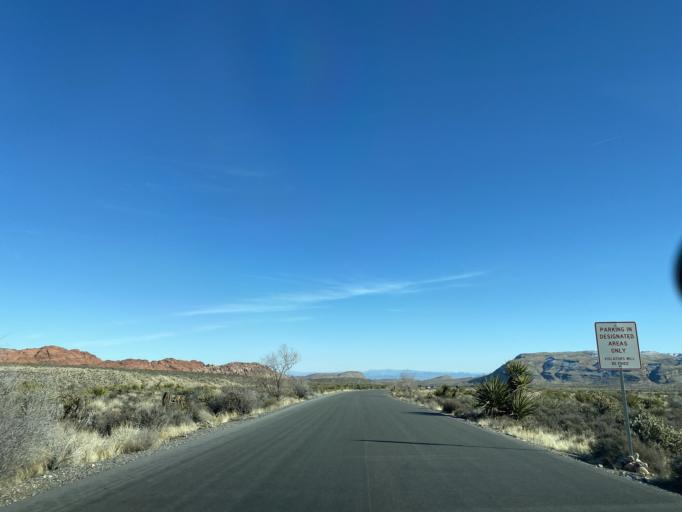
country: US
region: Nevada
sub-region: Clark County
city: Summerlin South
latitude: 36.1404
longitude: -115.4696
